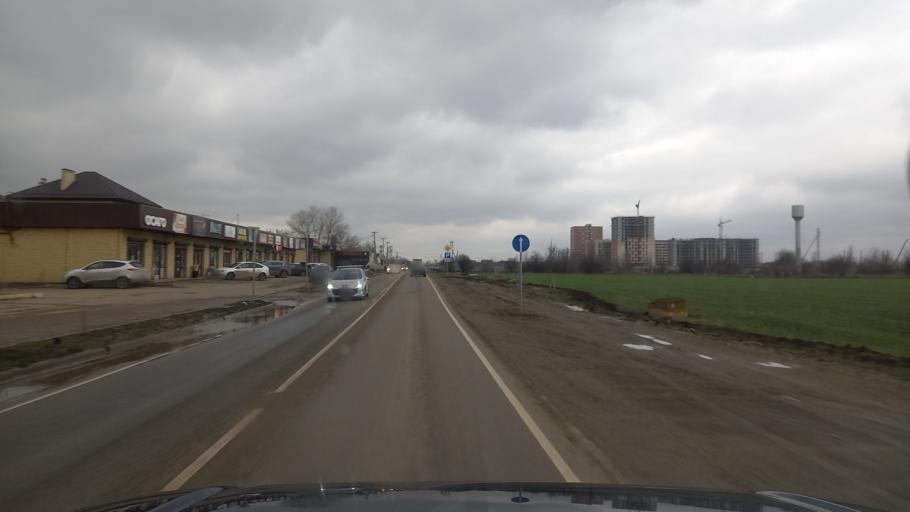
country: RU
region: Krasnodarskiy
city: Pashkovskiy
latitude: 45.0591
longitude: 39.1527
